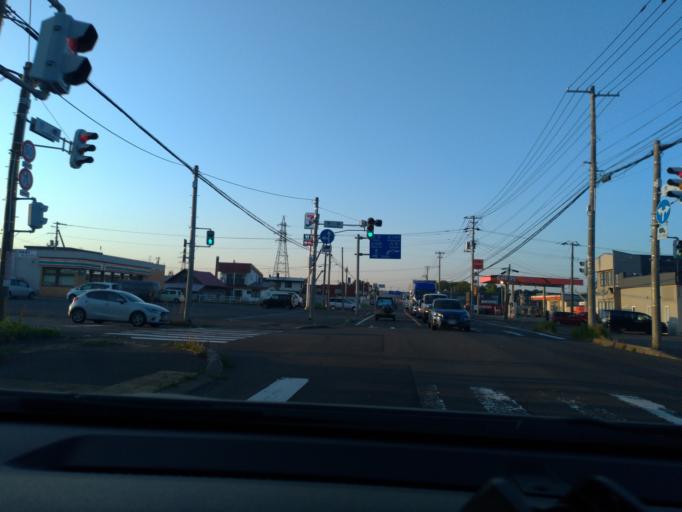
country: JP
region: Hokkaido
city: Tobetsu
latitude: 43.2095
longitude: 141.5189
